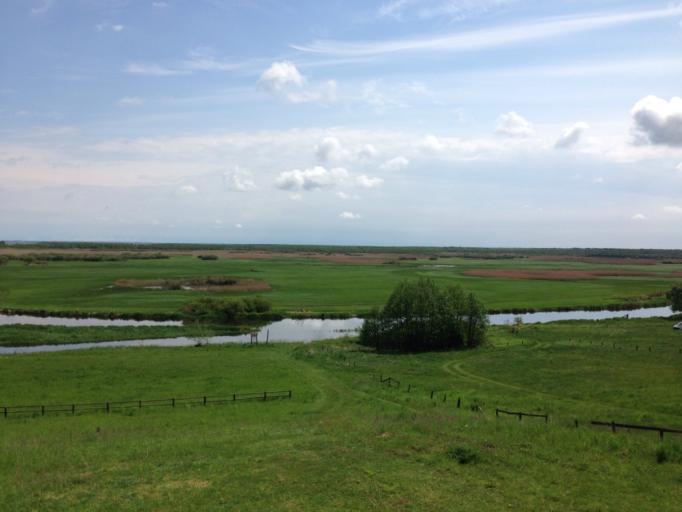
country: PL
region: Podlasie
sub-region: Powiat lomzynski
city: Wizna
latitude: 53.2753
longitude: 22.4571
